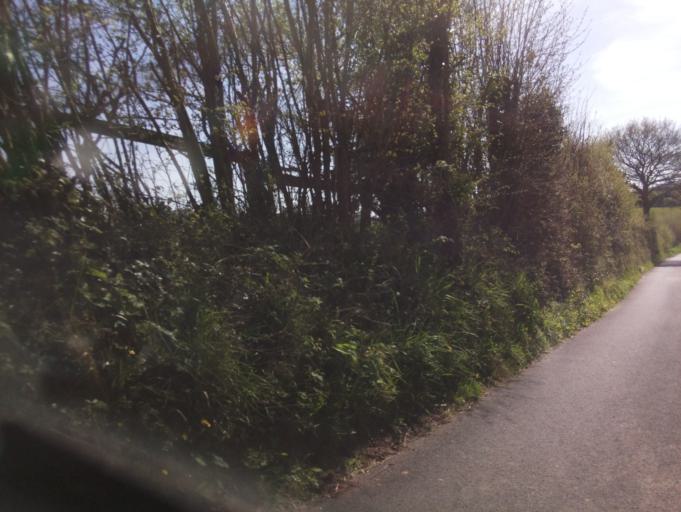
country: GB
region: Wales
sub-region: Monmouthshire
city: Llangwm
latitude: 51.7598
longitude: -2.8270
